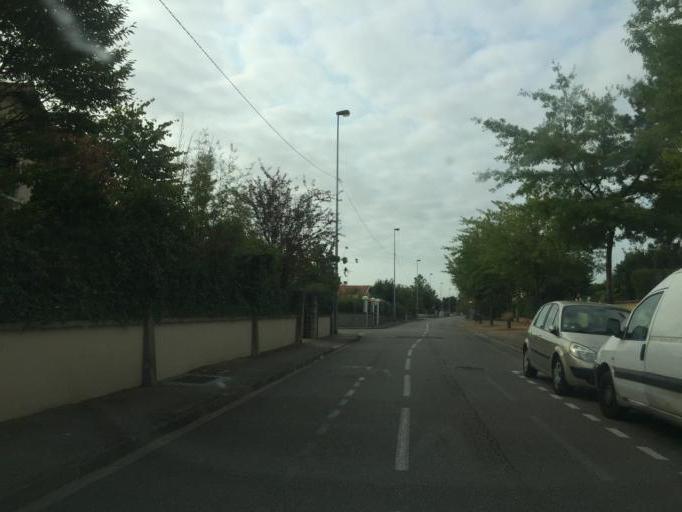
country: FR
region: Rhone-Alpes
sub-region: Departement du Rhone
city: Meyzieu
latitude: 45.7758
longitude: 5.0052
